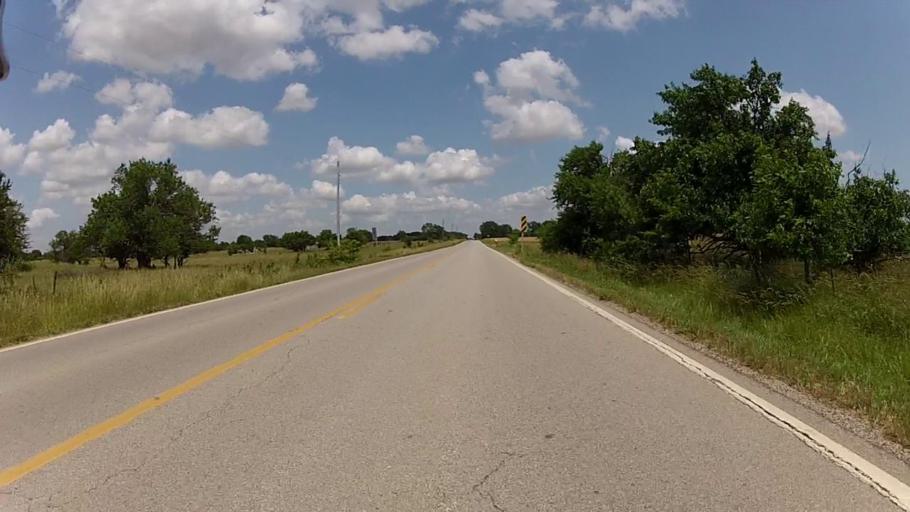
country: US
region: Kansas
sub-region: Labette County
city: Altamont
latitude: 37.1927
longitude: -95.3351
